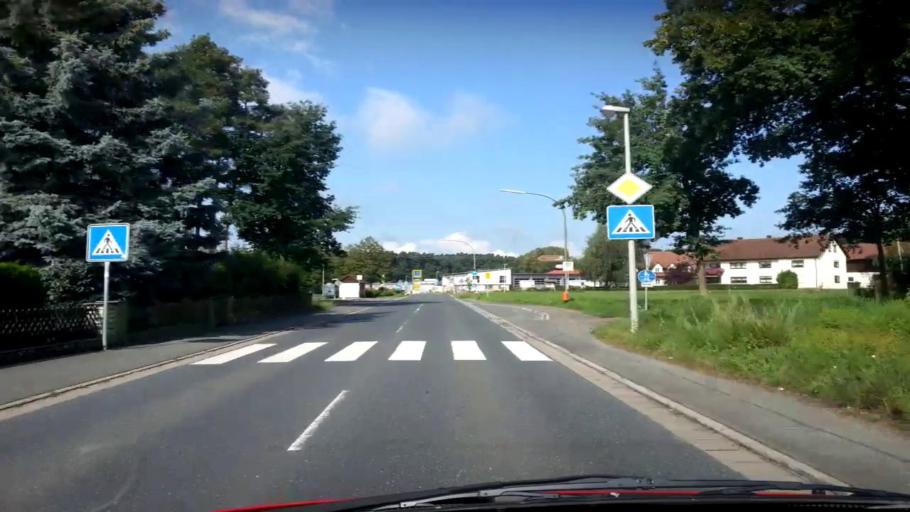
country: DE
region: Bavaria
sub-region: Upper Franconia
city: Hausen
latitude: 49.6929
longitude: 11.0230
